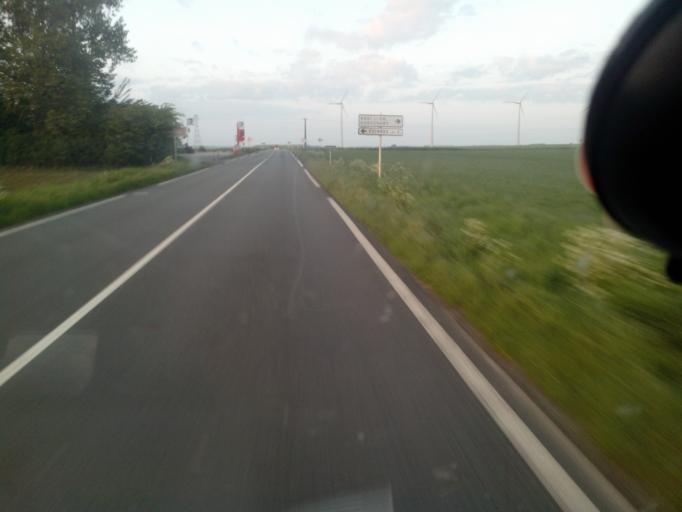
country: FR
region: Picardie
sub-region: Departement de la Somme
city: Crecy-en-Ponthieu
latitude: 50.2416
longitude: 1.9520
